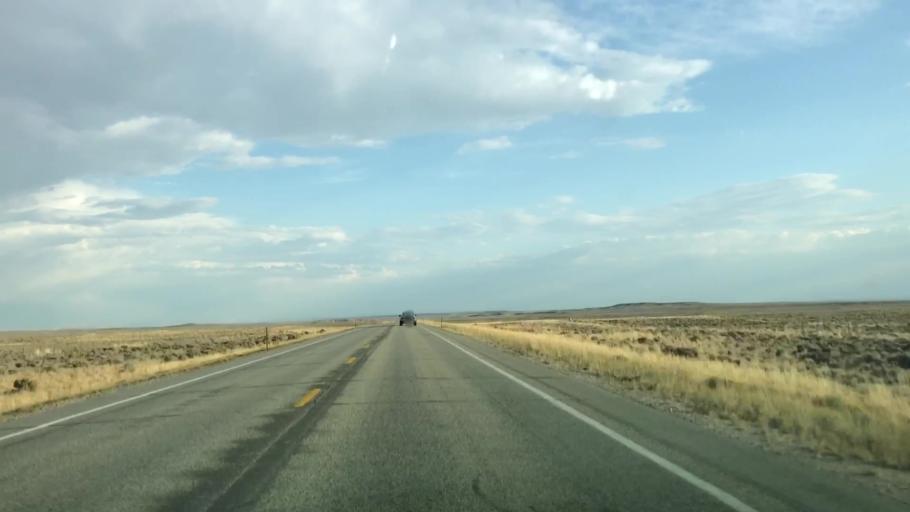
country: US
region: Wyoming
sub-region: Sublette County
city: Pinedale
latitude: 42.3899
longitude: -109.5399
